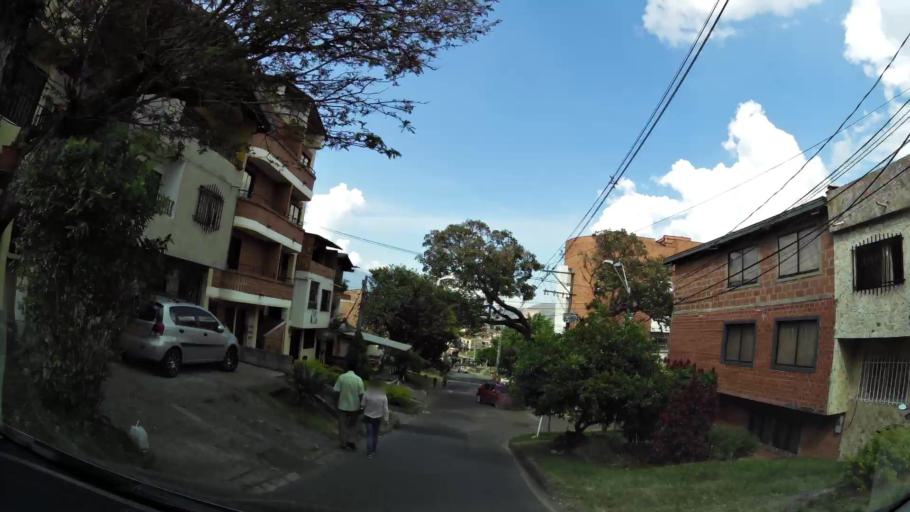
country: CO
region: Antioquia
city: Medellin
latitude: 6.2808
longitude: -75.5772
